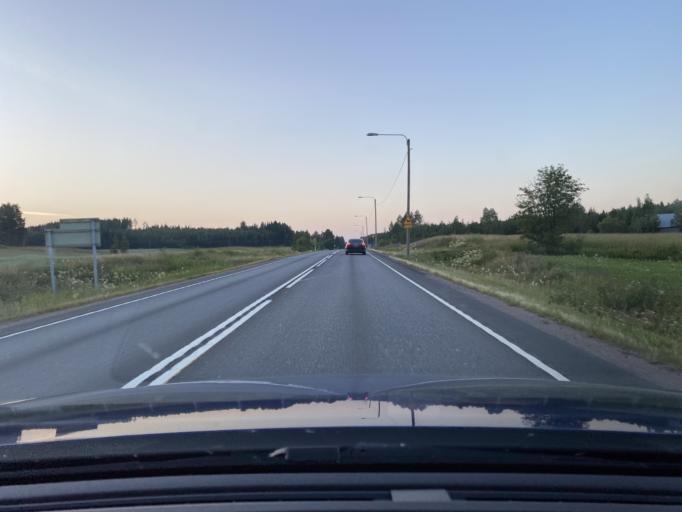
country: FI
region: Pirkanmaa
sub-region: Luoteis-Pirkanmaa
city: Ikaalinen
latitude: 61.8752
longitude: 22.9676
